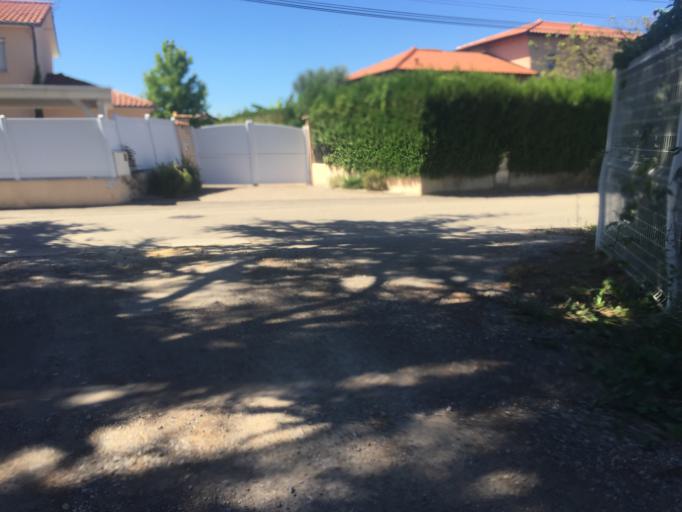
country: FR
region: Rhone-Alpes
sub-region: Departement de l'Ain
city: Beynost
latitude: 45.8306
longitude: 5.0014
